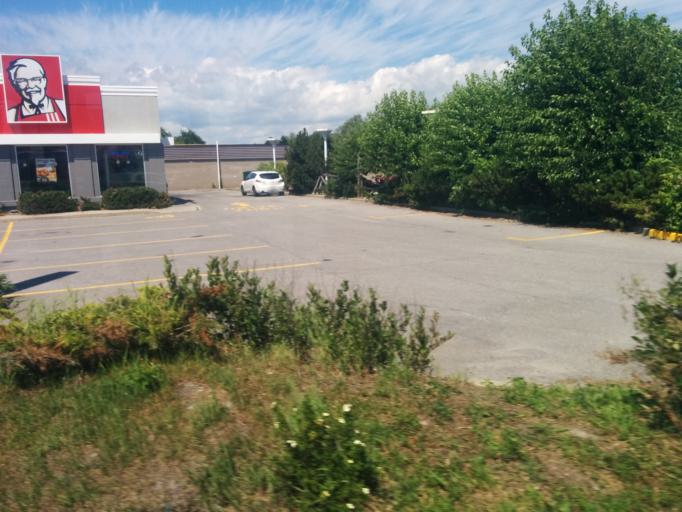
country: CA
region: Ontario
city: Kingston
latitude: 44.2502
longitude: -76.5305
